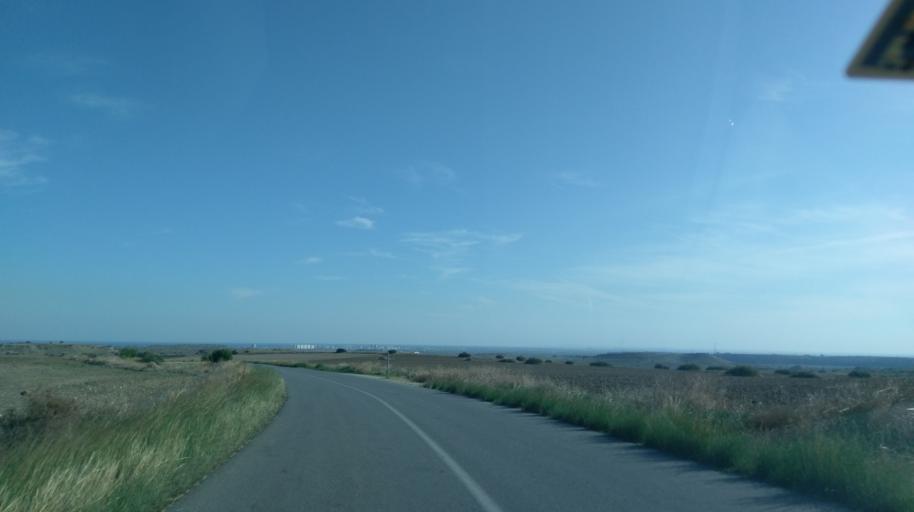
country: CY
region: Ammochostos
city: Trikomo
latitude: 35.3070
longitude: 33.8382
